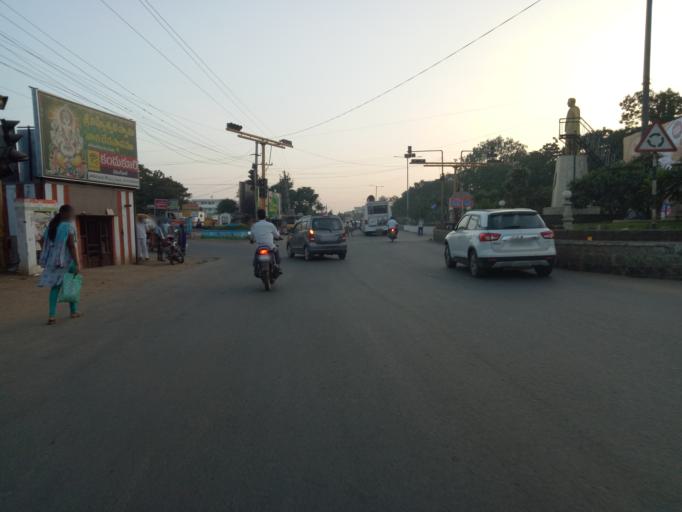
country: IN
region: Andhra Pradesh
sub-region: Nellore
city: Nellore
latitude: 14.4428
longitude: 79.9866
